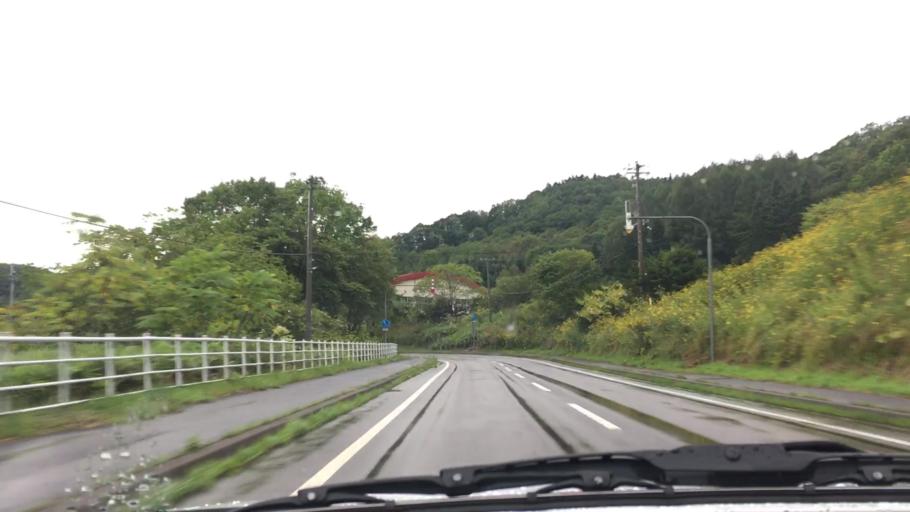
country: JP
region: Hokkaido
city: Niseko Town
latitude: 42.6491
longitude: 140.7358
